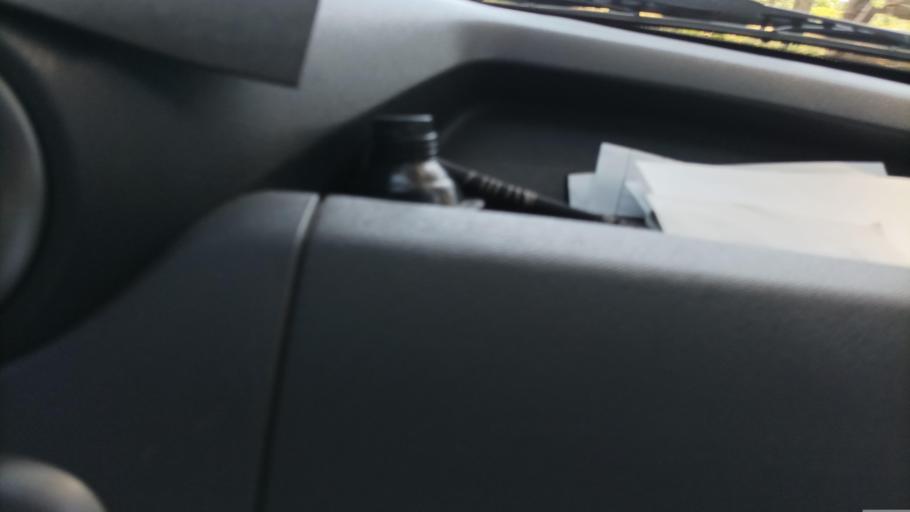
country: AR
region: Misiones
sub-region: Departamento de Apostoles
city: San Jose
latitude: -27.7868
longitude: -55.7041
